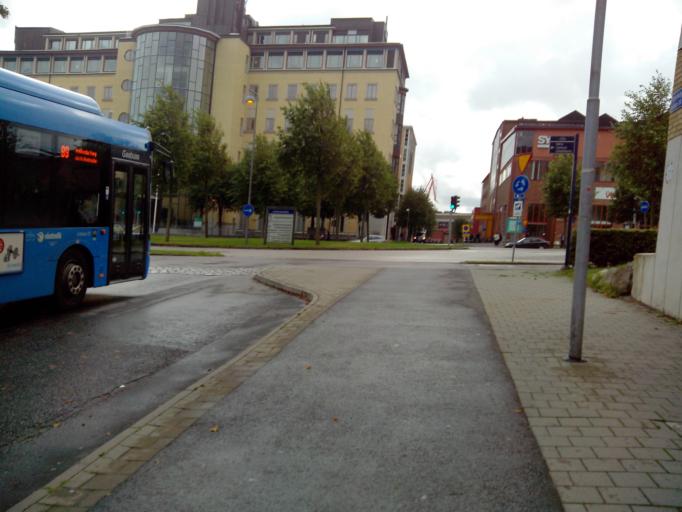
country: SE
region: Vaestra Goetaland
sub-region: Goteborg
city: Goeteborg
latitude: 57.7113
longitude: 11.9427
